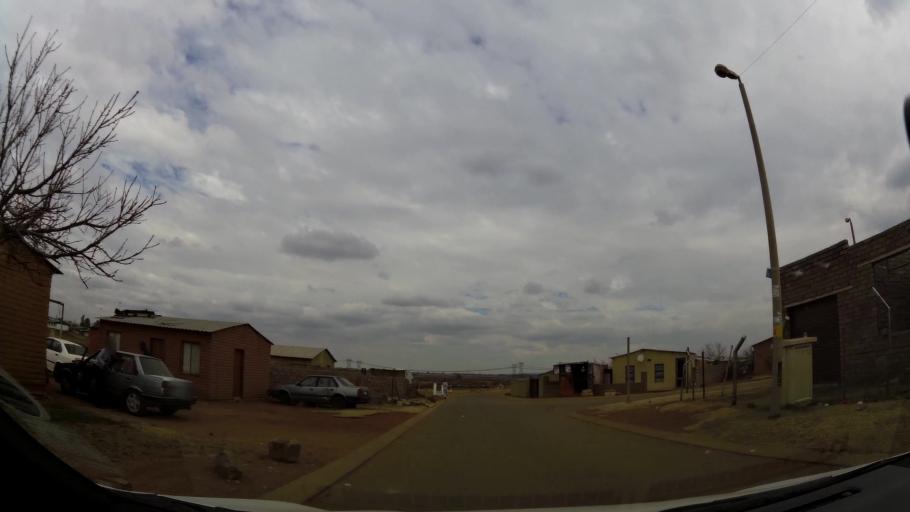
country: ZA
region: Gauteng
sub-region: Ekurhuleni Metropolitan Municipality
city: Germiston
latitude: -26.3883
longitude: 28.1220
